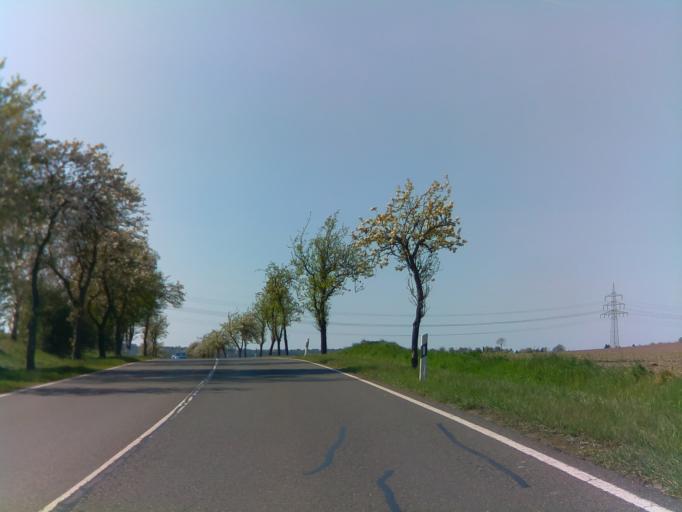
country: DE
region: Thuringia
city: Auma
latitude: 50.6836
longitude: 11.9162
